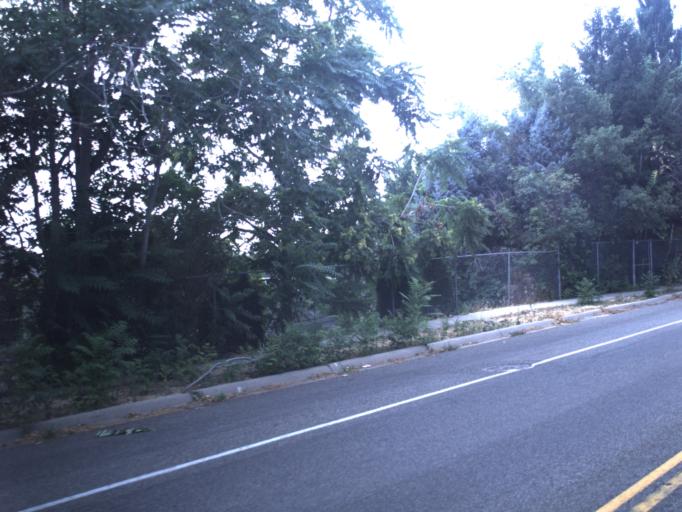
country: US
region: Utah
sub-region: Davis County
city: Farmington
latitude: 40.9588
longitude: -111.8833
